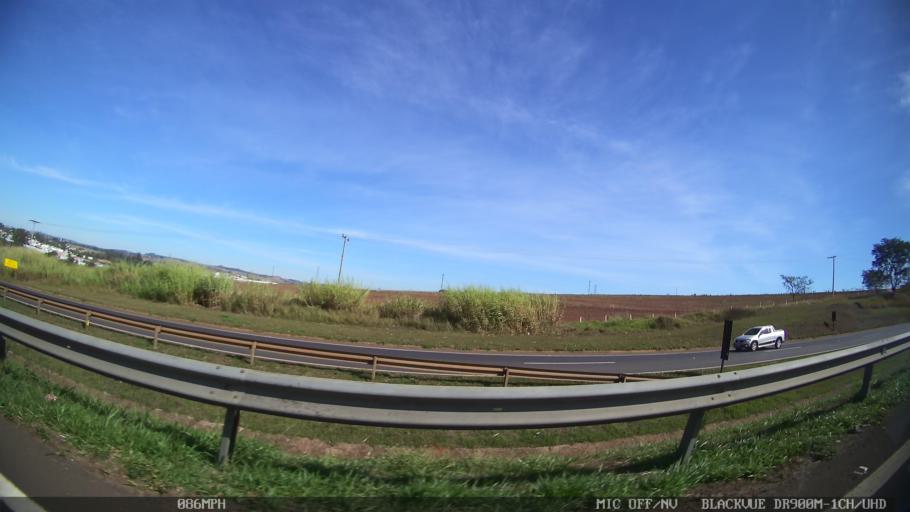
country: BR
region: Sao Paulo
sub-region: Leme
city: Leme
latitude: -22.1666
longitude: -47.3994
